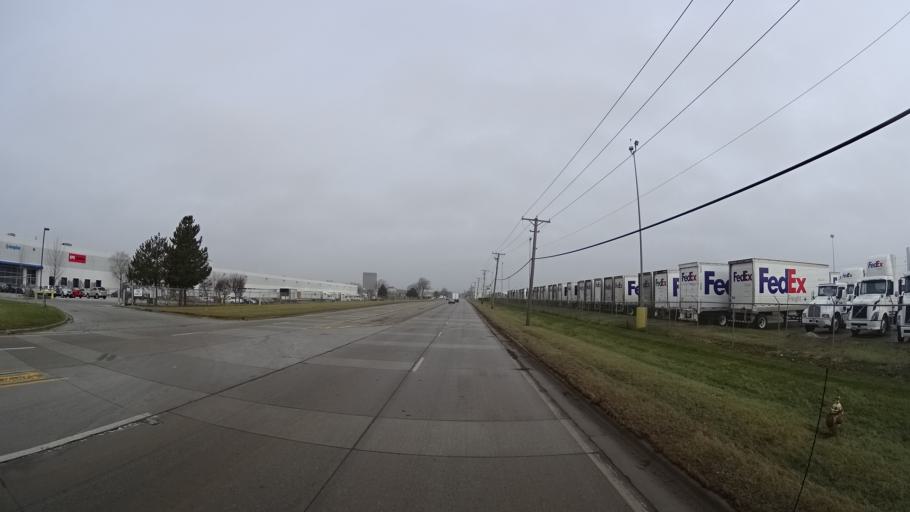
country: US
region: Illinois
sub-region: Cook County
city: Chicago Heights
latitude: 41.5167
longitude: -87.6162
